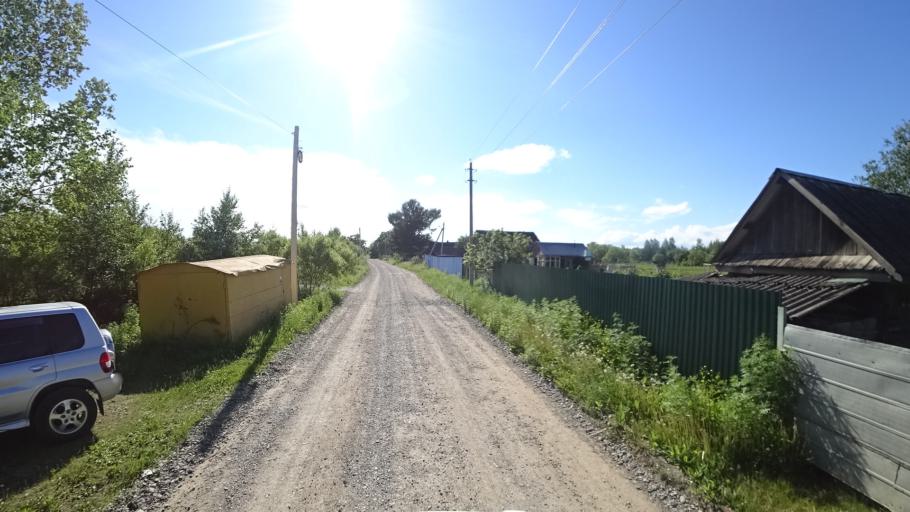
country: RU
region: Khabarovsk Krai
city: Khor
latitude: 47.8868
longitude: 135.0139
